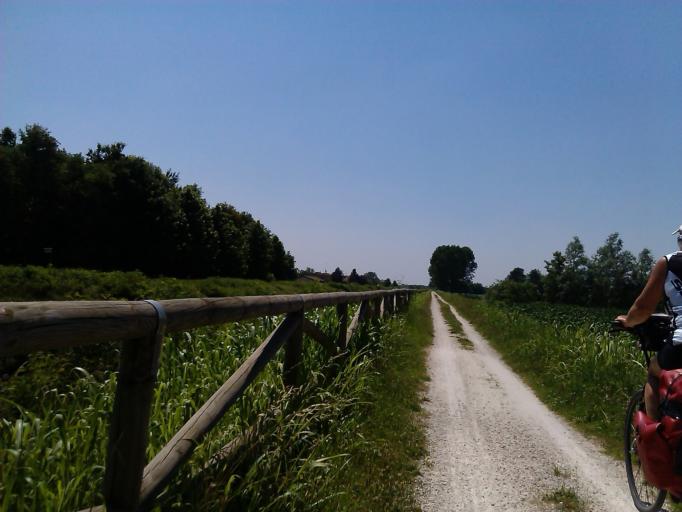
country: IT
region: Veneto
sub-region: Provincia di Padova
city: Loreggiola
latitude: 45.6222
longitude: 11.9268
